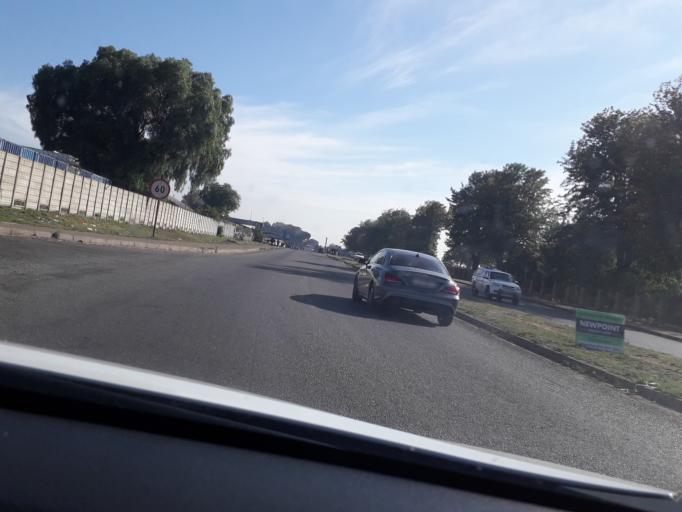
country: ZA
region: Gauteng
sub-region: Ekurhuleni Metropolitan Municipality
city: Boksburg
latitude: -26.1700
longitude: 28.2041
